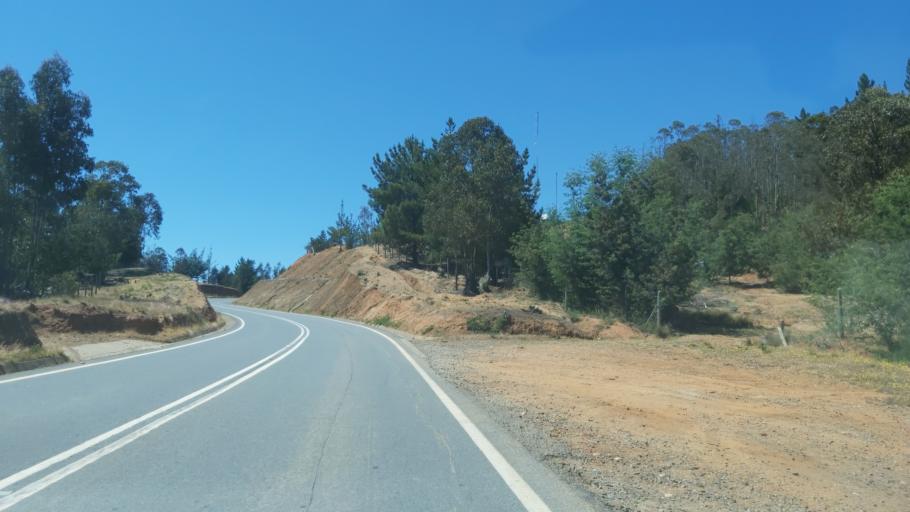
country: CL
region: Maule
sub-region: Provincia de Talca
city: Constitucion
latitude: -34.9153
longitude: -71.9945
